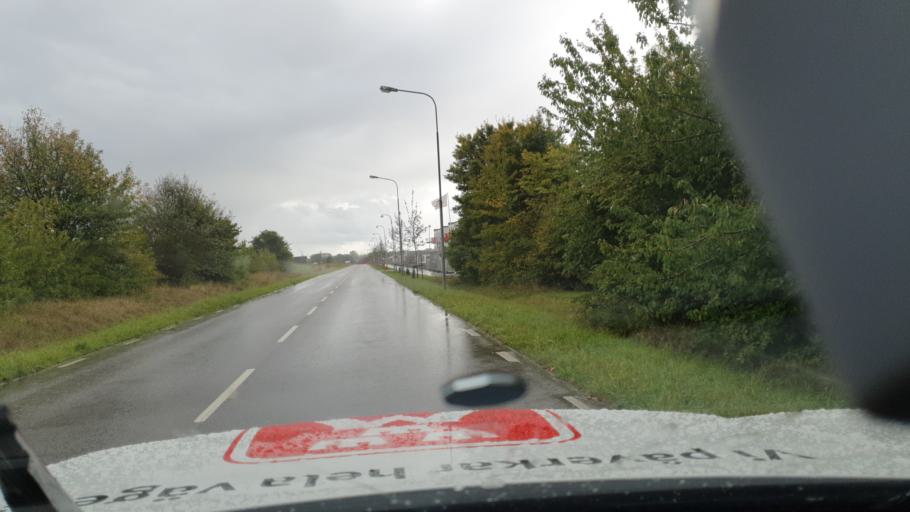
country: SE
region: Skane
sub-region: Vellinge Kommun
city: Vellinge
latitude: 55.4755
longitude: 13.0421
